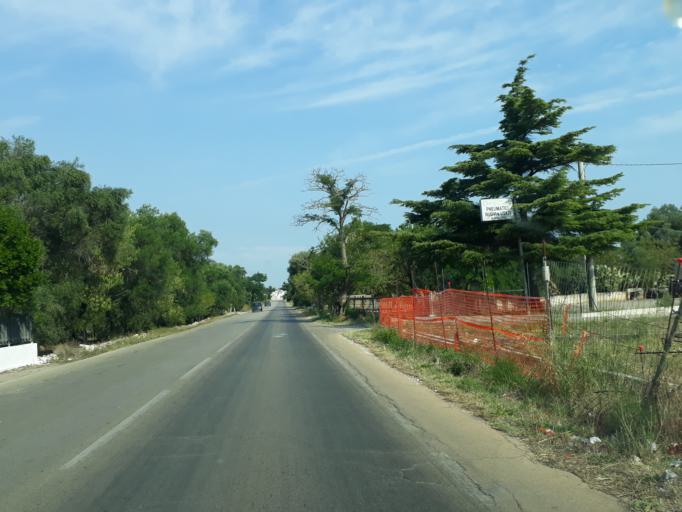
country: IT
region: Apulia
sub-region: Provincia di Brindisi
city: Carovigno
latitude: 40.6882
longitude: 17.6763
